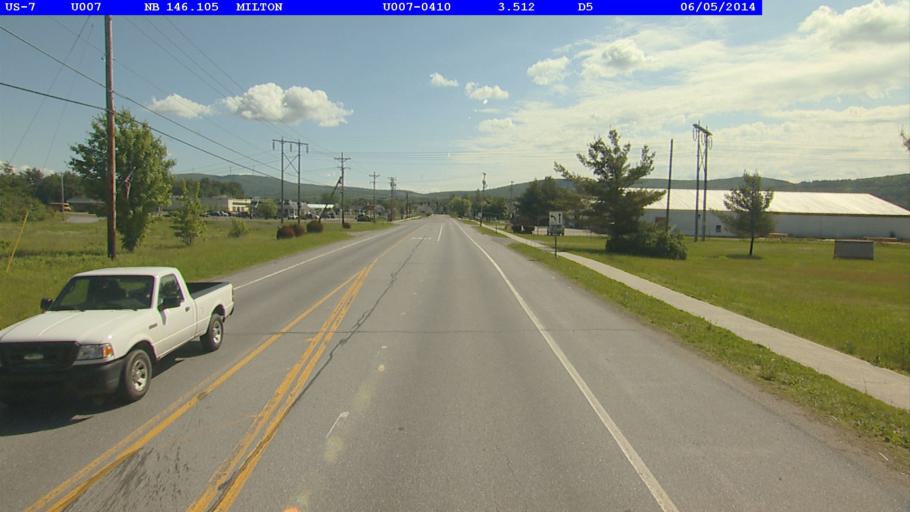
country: US
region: Vermont
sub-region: Chittenden County
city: Milton
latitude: 44.6214
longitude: -73.1254
